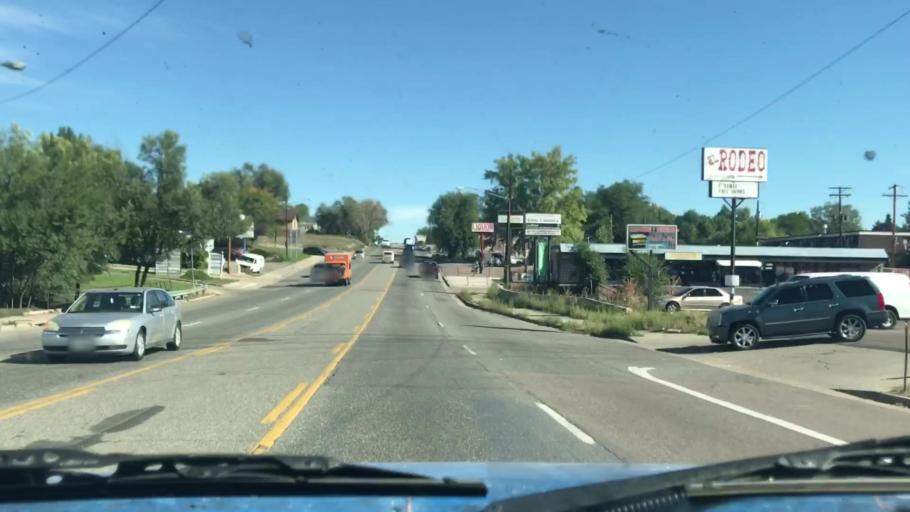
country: US
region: Colorado
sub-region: Jefferson County
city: Edgewater
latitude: 39.7280
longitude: -105.0532
